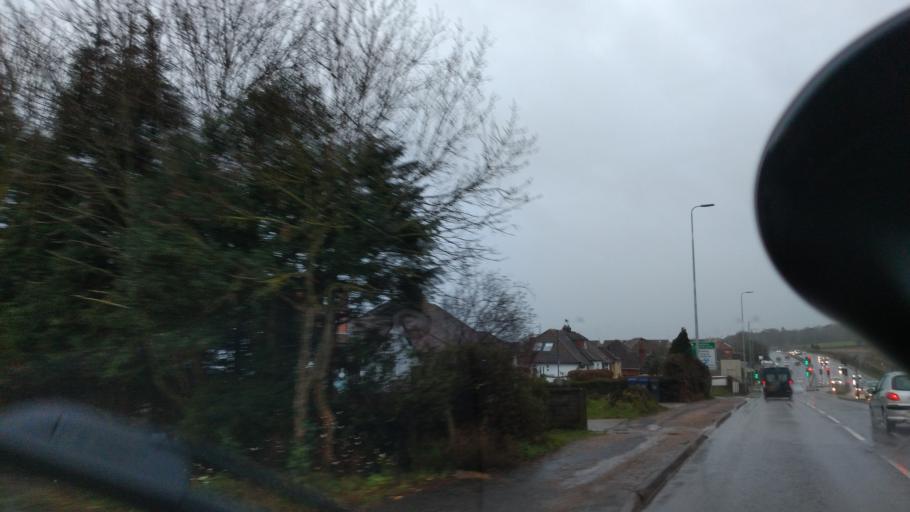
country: GB
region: England
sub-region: West Sussex
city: Lancing
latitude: 50.8374
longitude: -0.3343
